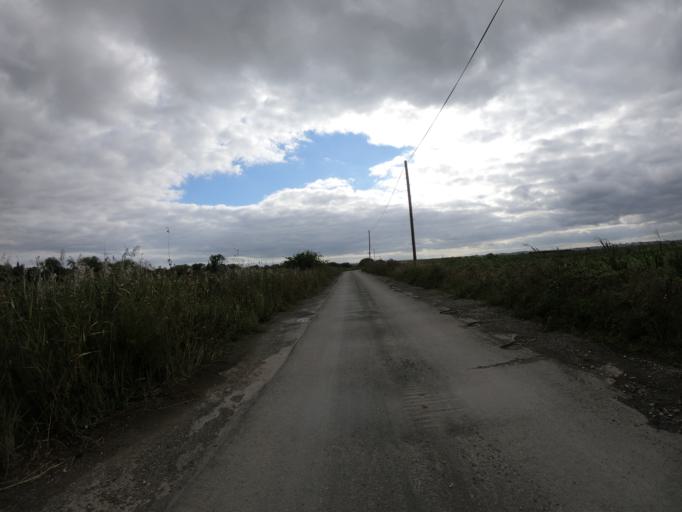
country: GB
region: England
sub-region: Essex
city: Purfleet
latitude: 51.4712
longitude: 0.2188
